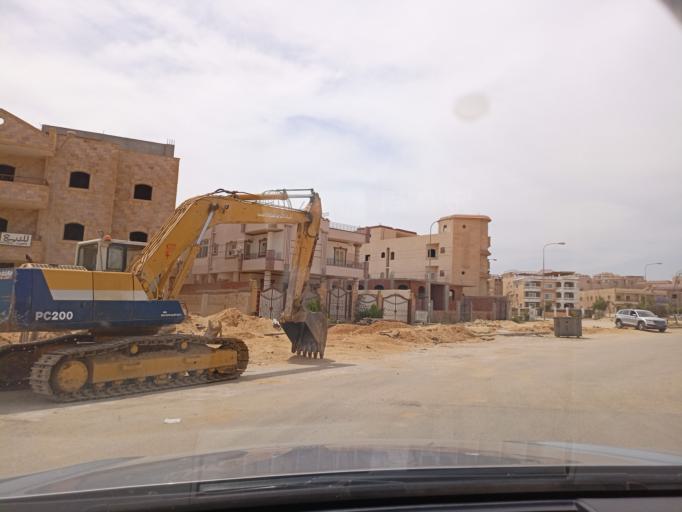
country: EG
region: Muhafazat al Qalyubiyah
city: Al Khankah
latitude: 30.2321
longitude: 31.4934
